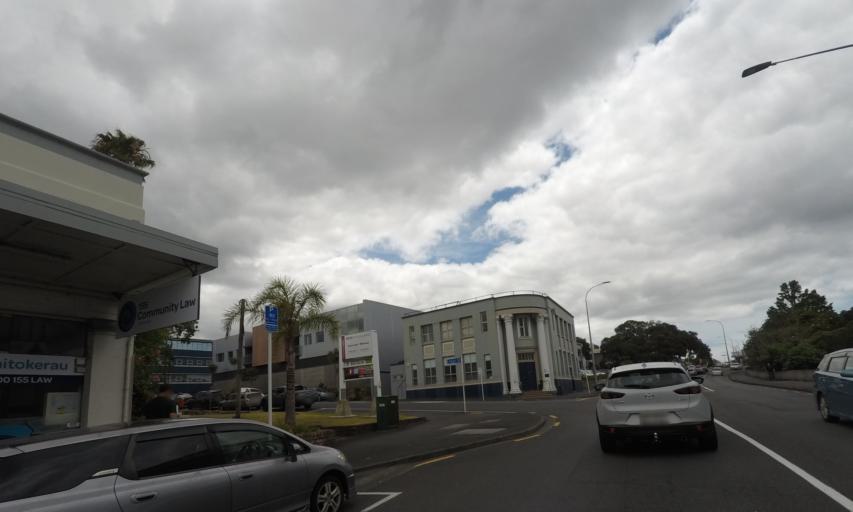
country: NZ
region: Northland
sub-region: Whangarei
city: Whangarei
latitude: -35.7234
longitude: 174.3199
